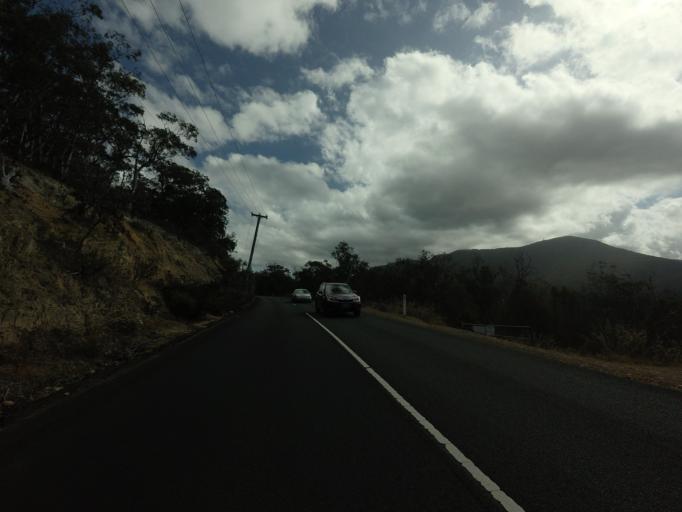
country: AU
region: Tasmania
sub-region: Hobart
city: Dynnyrne
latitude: -42.9014
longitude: 147.2920
